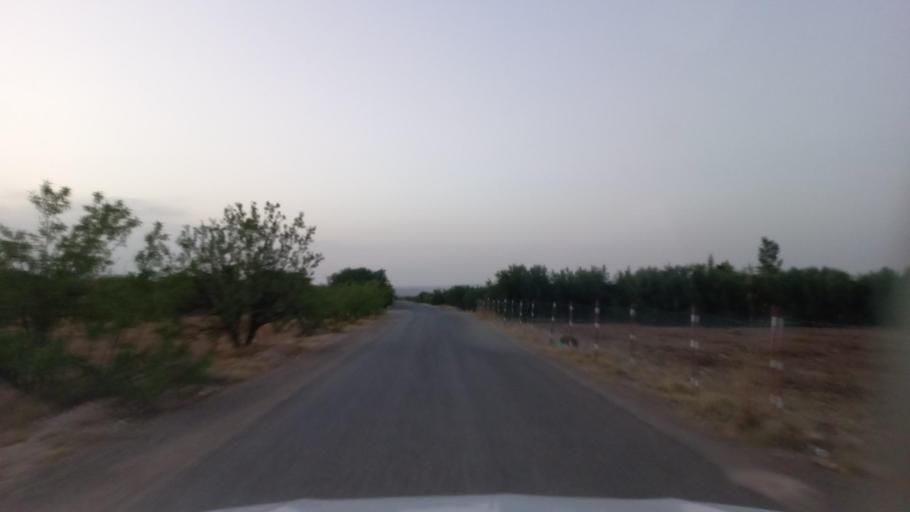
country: TN
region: Al Qasrayn
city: Kasserine
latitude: 35.2768
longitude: 9.0289
